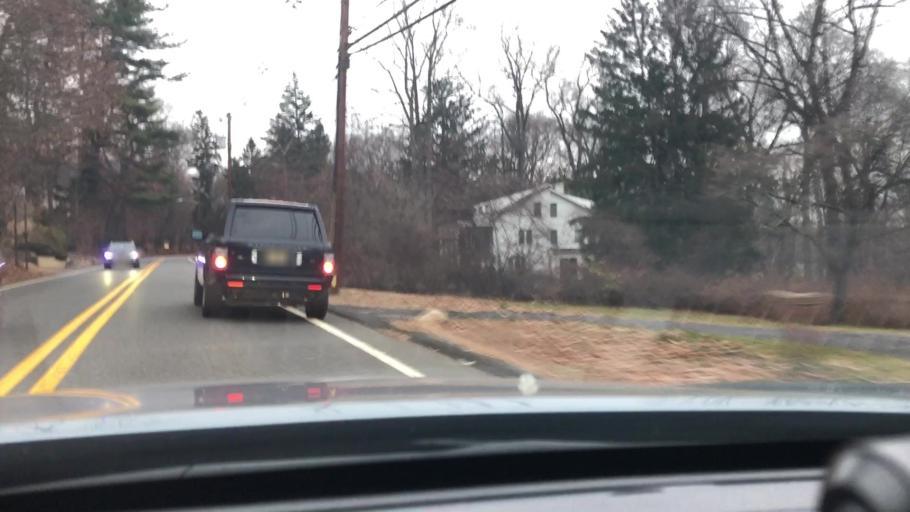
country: US
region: New Jersey
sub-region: Bergen County
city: Woodcliff Lake
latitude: 41.0027
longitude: -74.0751
